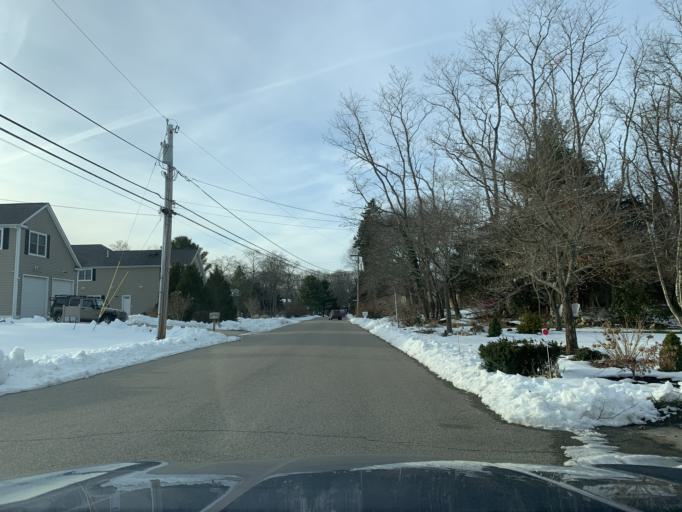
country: US
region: Rhode Island
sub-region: Washington County
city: North Kingstown
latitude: 41.5900
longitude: -71.4392
